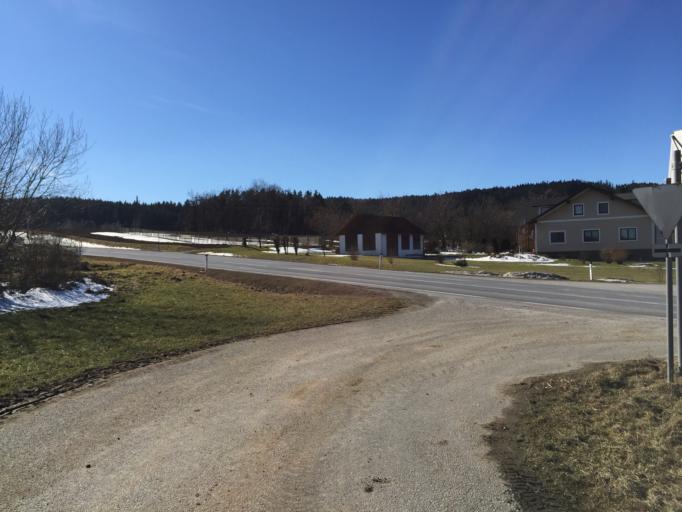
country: AT
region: Lower Austria
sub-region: Politischer Bezirk Gmund
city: Weitra
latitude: 48.6657
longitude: 14.9366
